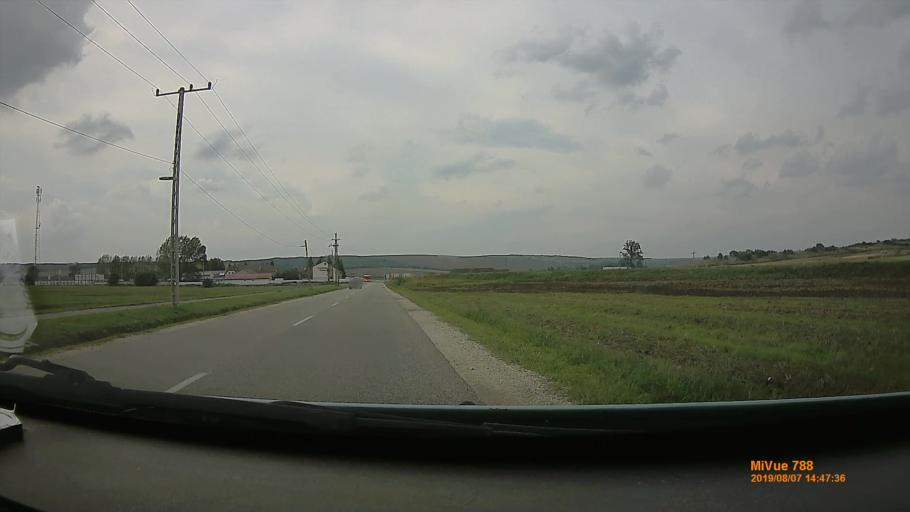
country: HU
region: Borsod-Abauj-Zemplen
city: Halmaj
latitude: 48.2509
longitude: 20.9847
